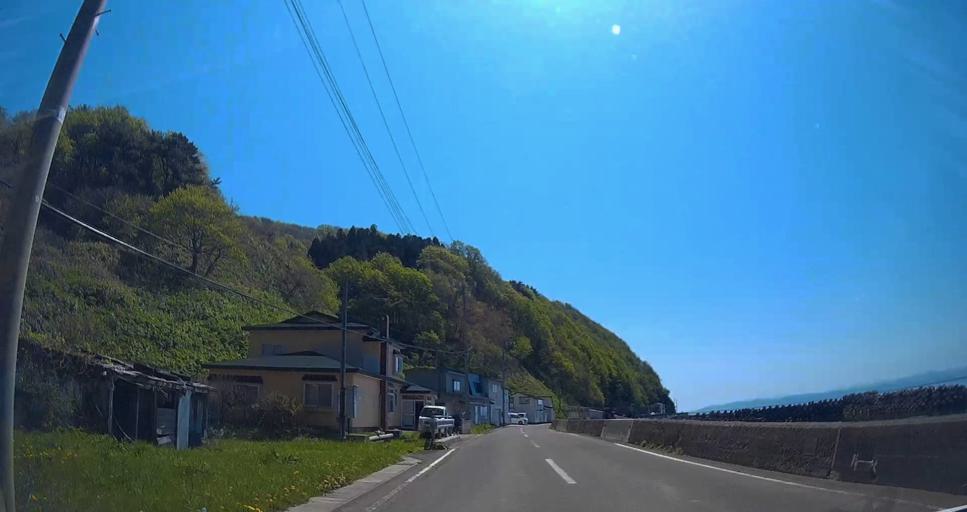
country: JP
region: Aomori
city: Aomori Shi
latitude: 41.1329
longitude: 140.7935
